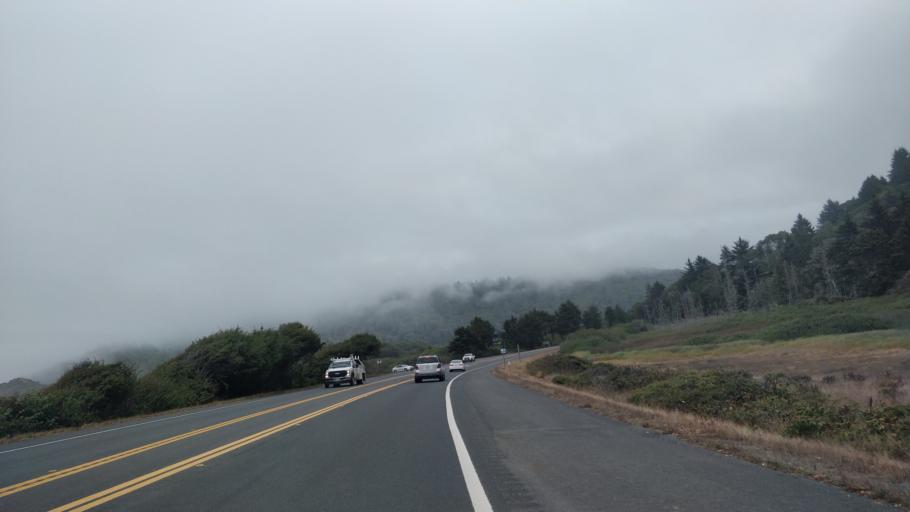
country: US
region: California
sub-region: Humboldt County
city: Westhaven-Moonstone
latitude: 41.2824
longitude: -124.0921
